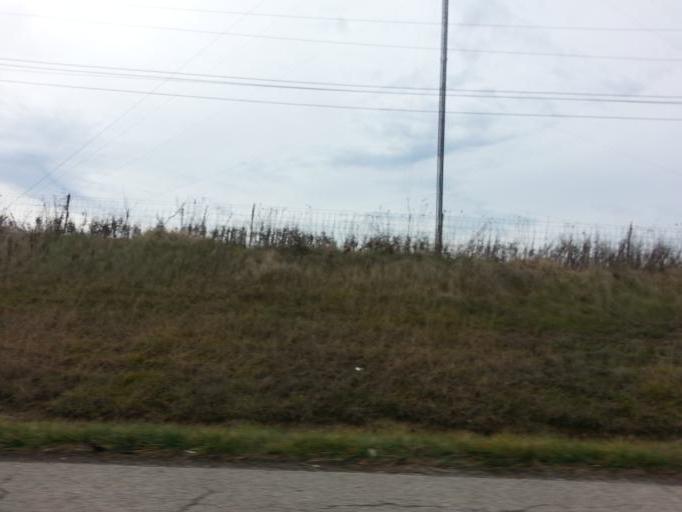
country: US
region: Indiana
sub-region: Decatur County
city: Greensburg
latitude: 39.3588
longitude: -85.4643
